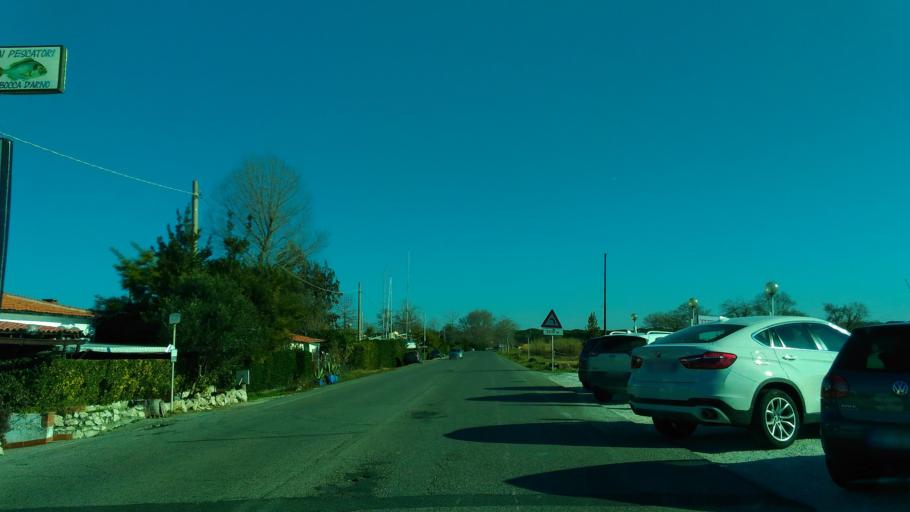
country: IT
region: Tuscany
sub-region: Province of Pisa
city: Marina di Pisa
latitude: 43.6761
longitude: 10.3132
